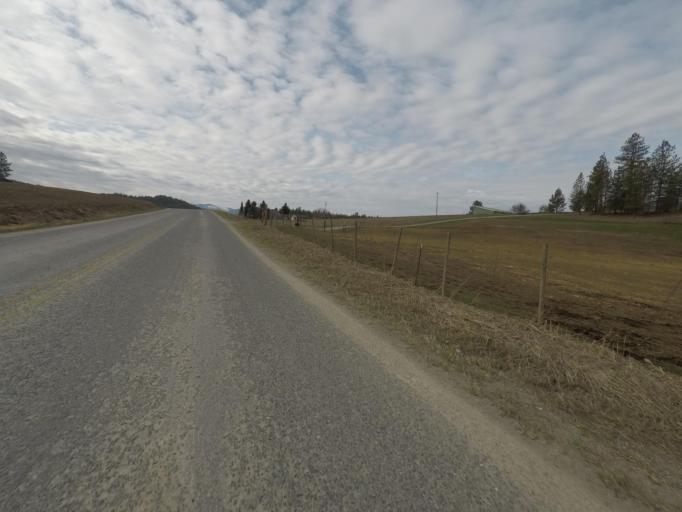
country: US
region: Washington
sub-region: Stevens County
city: Colville
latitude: 48.5246
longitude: -117.8812
